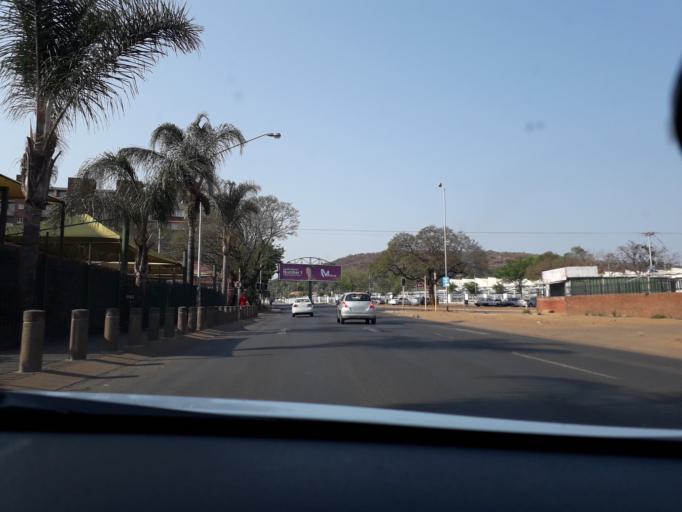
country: ZA
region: Gauteng
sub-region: City of Tshwane Metropolitan Municipality
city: Pretoria
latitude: -25.7576
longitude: 28.1915
